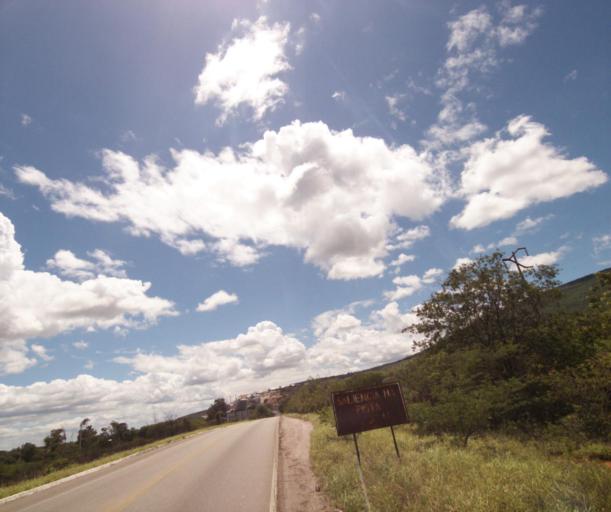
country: BR
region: Bahia
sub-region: Brumado
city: Brumado
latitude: -14.2380
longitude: -41.7162
